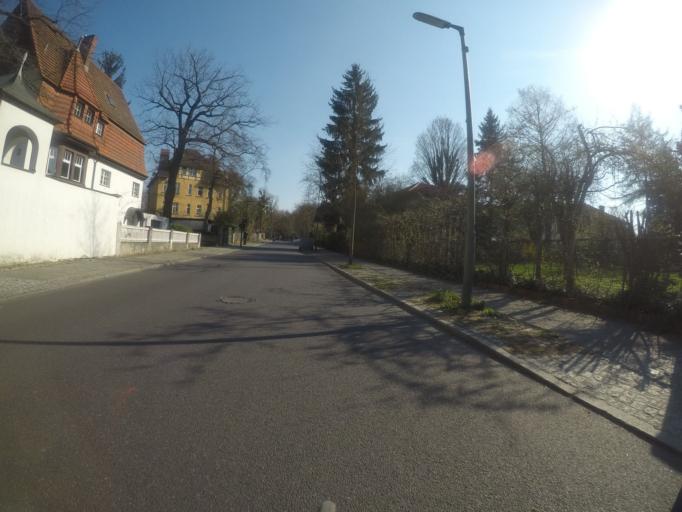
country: DE
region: Berlin
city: Wannsee
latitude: 52.3984
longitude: 13.1431
